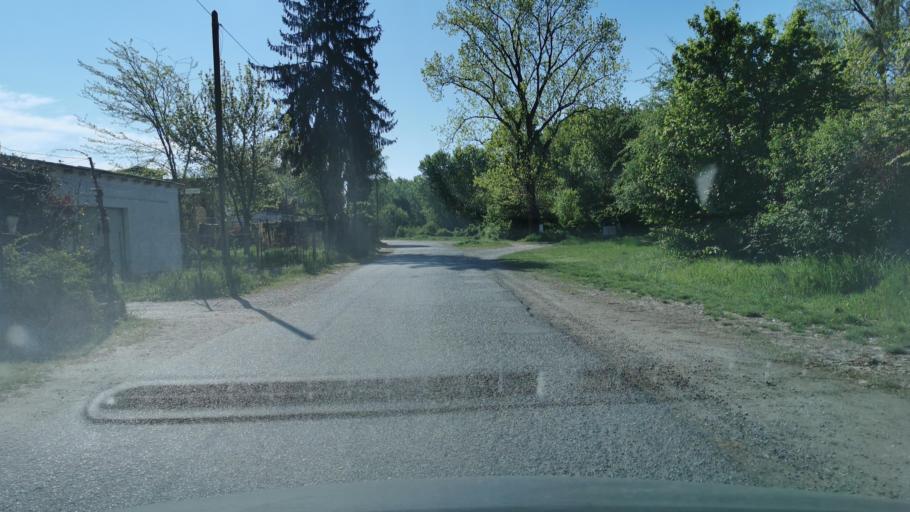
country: IT
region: Lombardy
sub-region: Provincia di Cremona
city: Cremona
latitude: 45.1194
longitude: 10.0095
